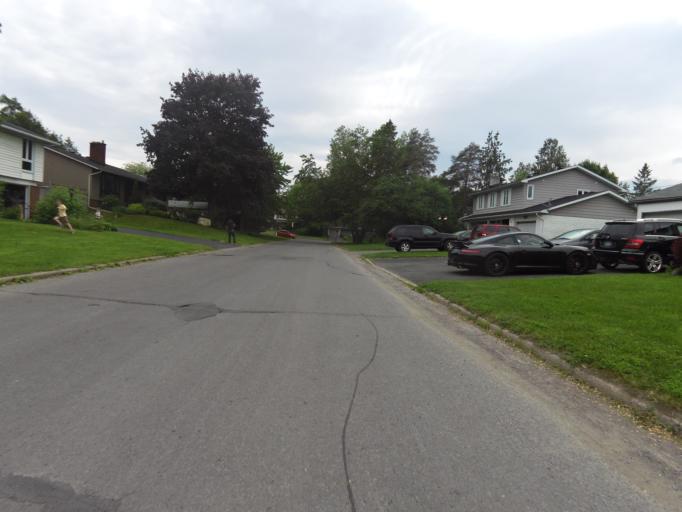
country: CA
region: Ontario
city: Ottawa
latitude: 45.3610
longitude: -75.7296
